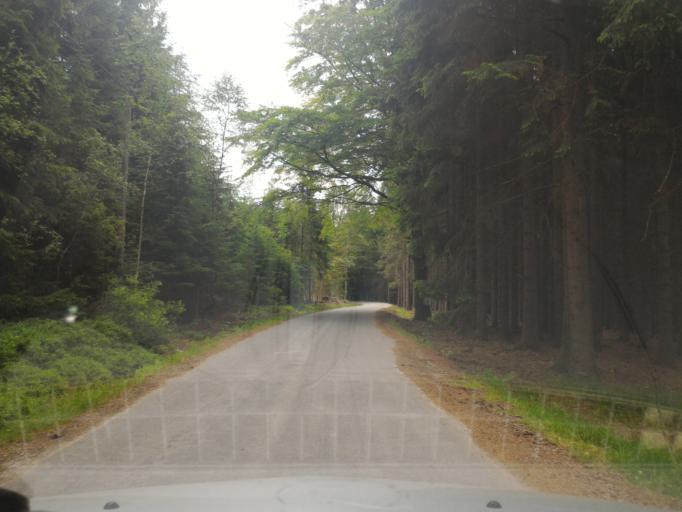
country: CZ
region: Vysocina
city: Batelov
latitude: 49.2329
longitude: 15.3754
